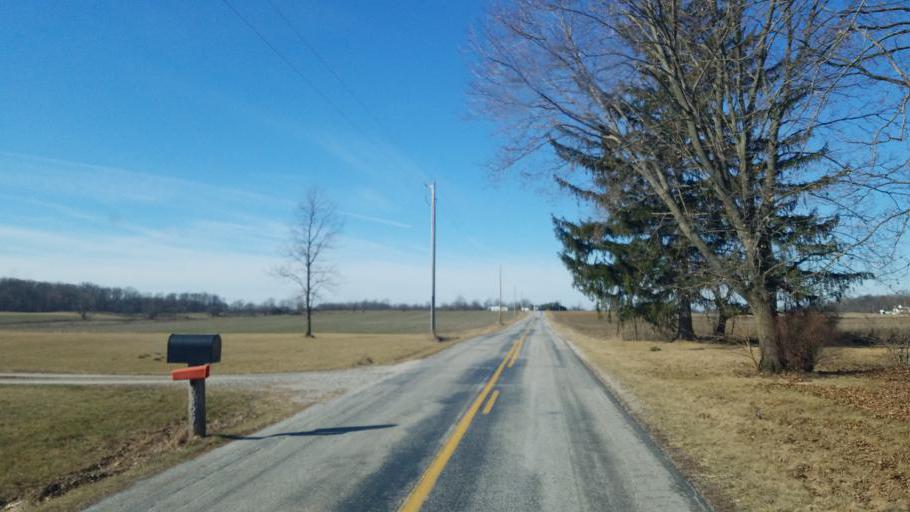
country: US
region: Ohio
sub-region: Union County
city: Richwood
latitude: 40.5145
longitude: -83.3030
